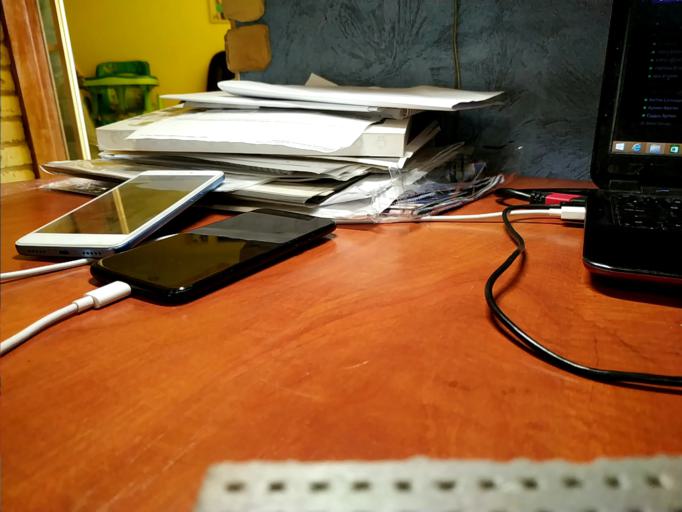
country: RU
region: Tverskaya
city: Spirovo
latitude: 57.4213
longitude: 35.1031
